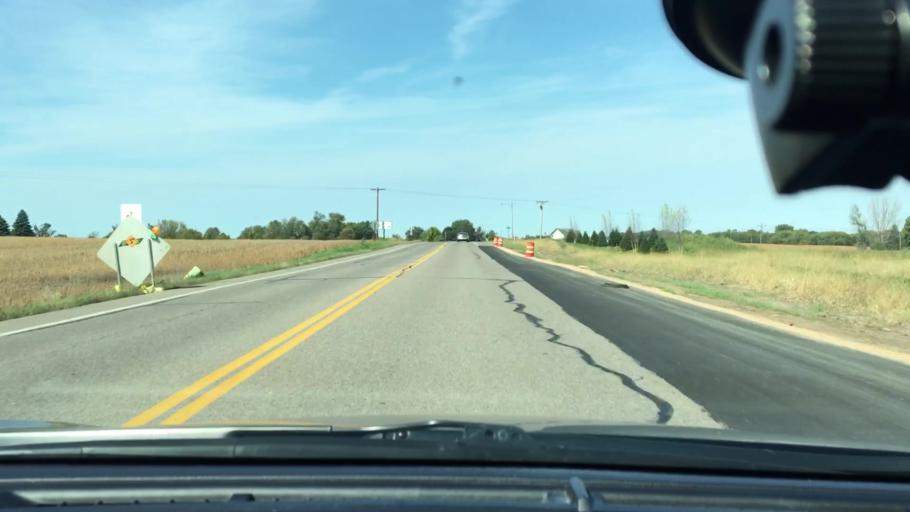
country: US
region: Minnesota
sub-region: Hennepin County
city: Corcoran
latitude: 45.0882
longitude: -93.5312
